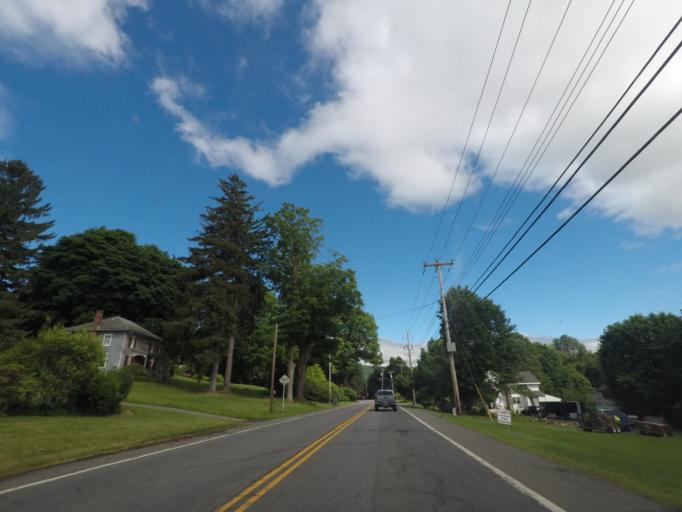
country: US
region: New York
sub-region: Columbia County
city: Philmont
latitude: 42.1801
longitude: -73.5298
